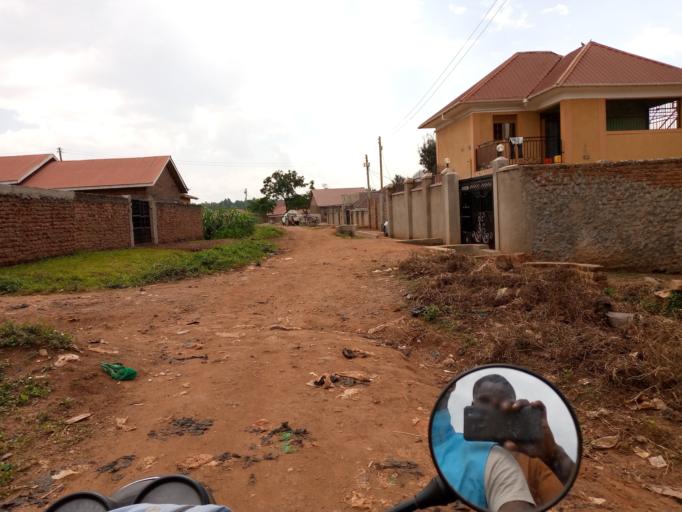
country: UG
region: Eastern Region
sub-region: Mbale District
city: Mbale
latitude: 1.0849
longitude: 34.1607
